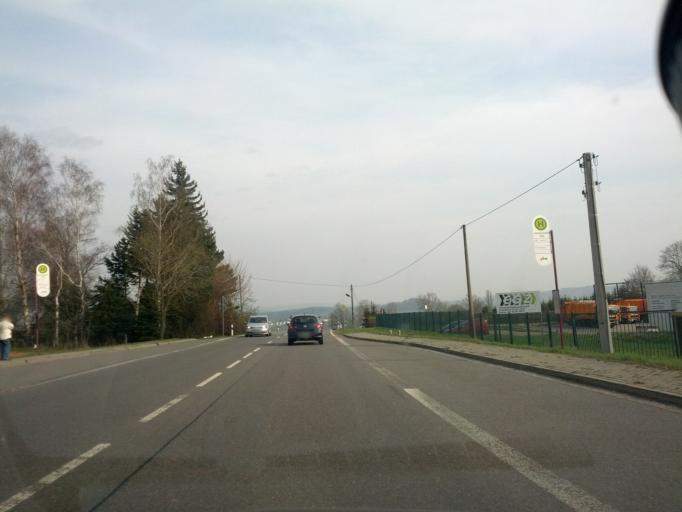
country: DE
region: Saxony
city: Reinsdorf
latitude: 50.6797
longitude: 12.5862
